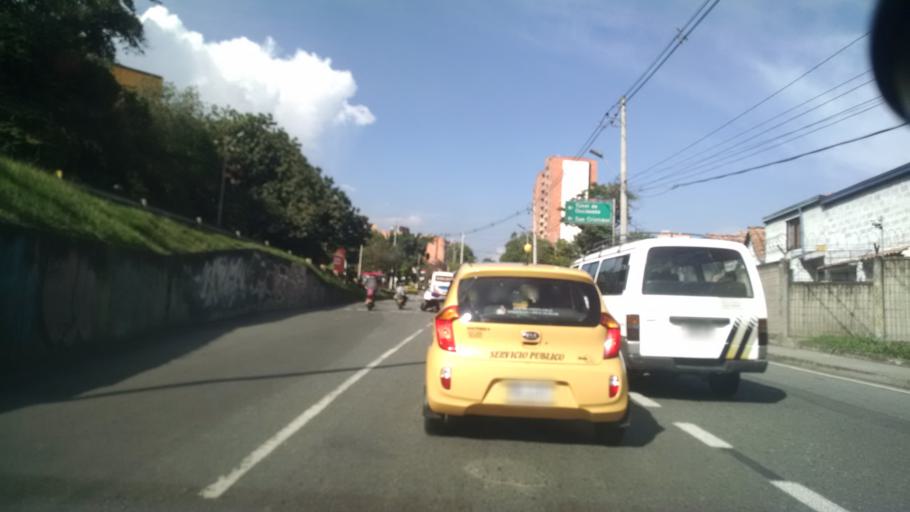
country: CO
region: Antioquia
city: Medellin
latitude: 6.2765
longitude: -75.5899
